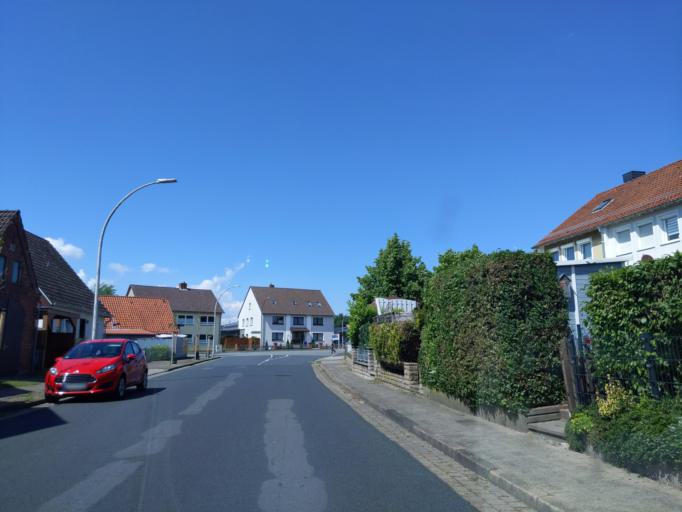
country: DE
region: Lower Saxony
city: Walsrode
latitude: 52.8645
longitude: 9.6054
